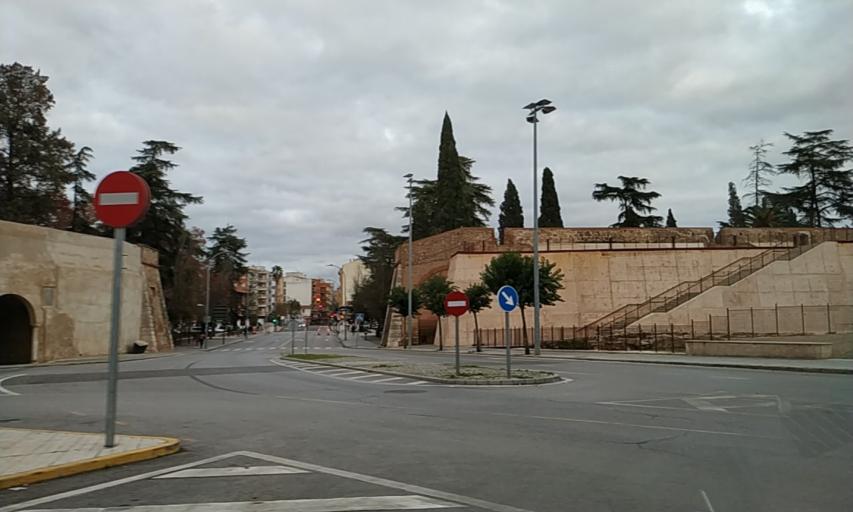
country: ES
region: Extremadura
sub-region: Provincia de Badajoz
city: Badajoz
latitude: 38.8778
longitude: -6.9646
